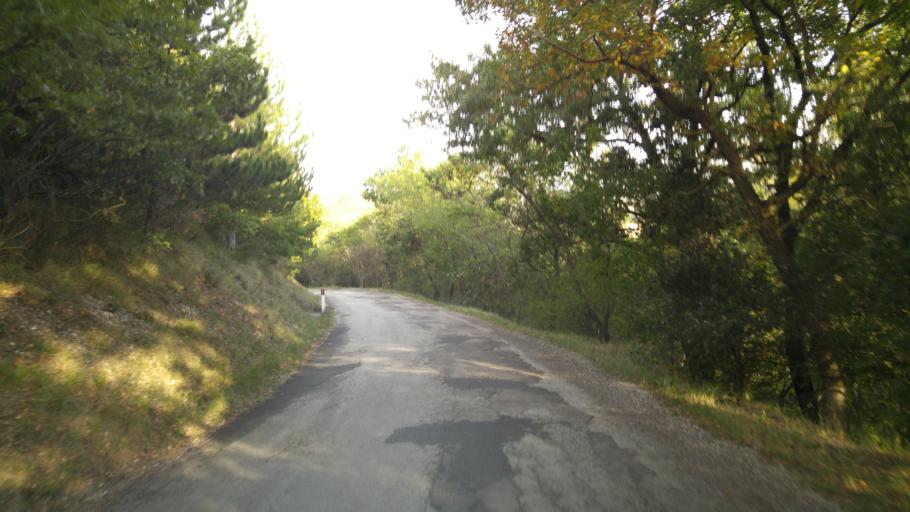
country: IT
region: The Marches
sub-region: Provincia di Pesaro e Urbino
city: Cagli
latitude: 43.5511
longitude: 12.6396
